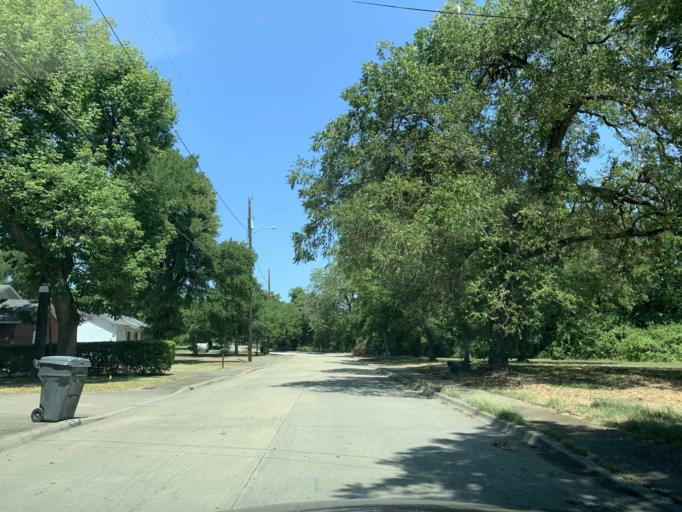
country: US
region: Texas
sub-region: Dallas County
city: Hutchins
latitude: 32.6836
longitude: -96.7937
